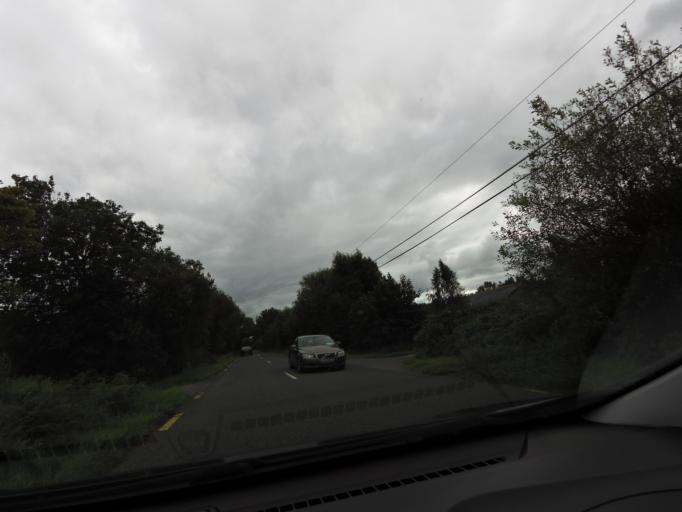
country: IE
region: Leinster
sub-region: Uibh Fhaili
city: Banagher
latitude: 53.2809
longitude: -8.0663
